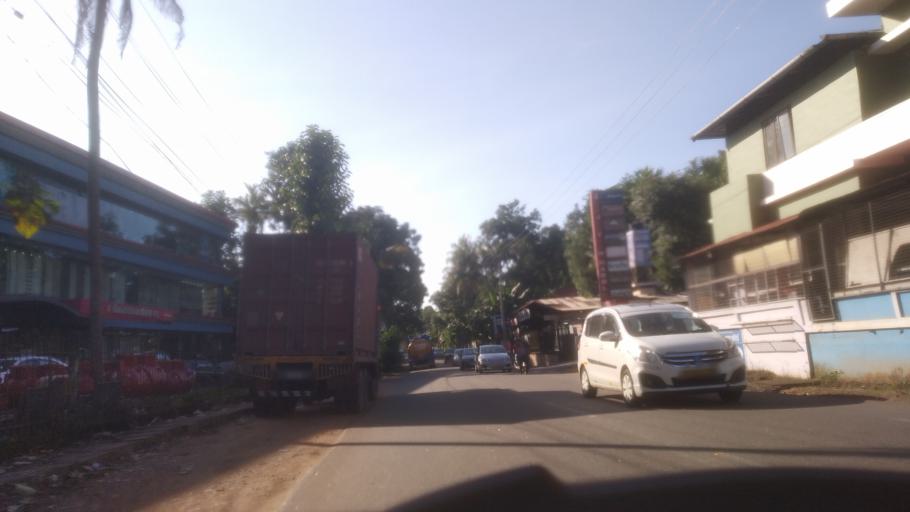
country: IN
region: Kerala
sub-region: Ernakulam
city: Ramamangalam
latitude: 9.9773
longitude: 76.4959
